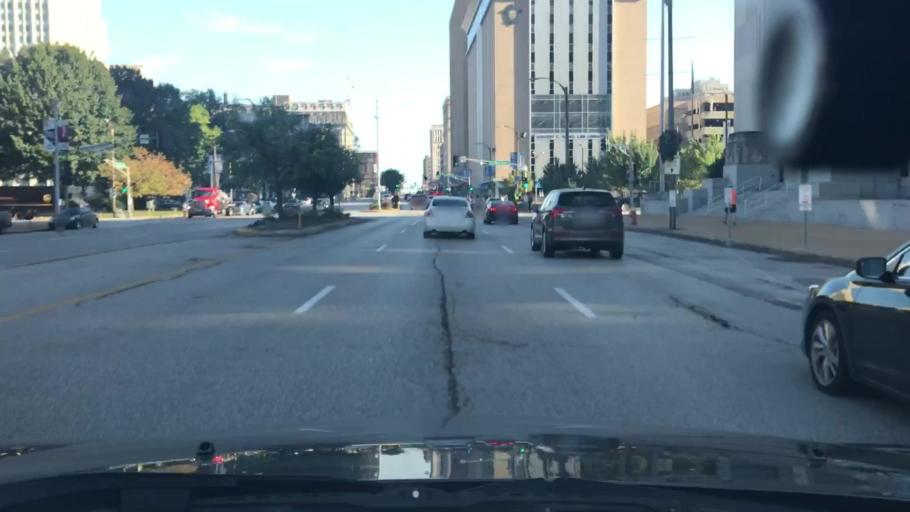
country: US
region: Missouri
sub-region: City of Saint Louis
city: St. Louis
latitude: 38.6268
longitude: -90.1984
